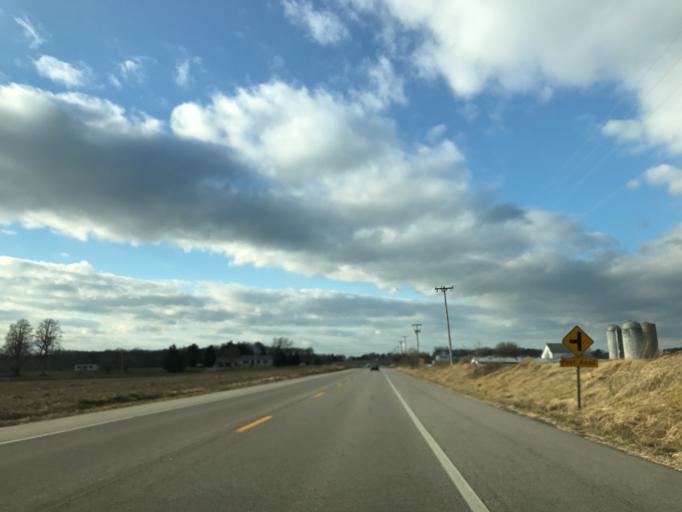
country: US
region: Maryland
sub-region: Cecil County
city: Rising Sun
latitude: 39.6720
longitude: -76.0210
